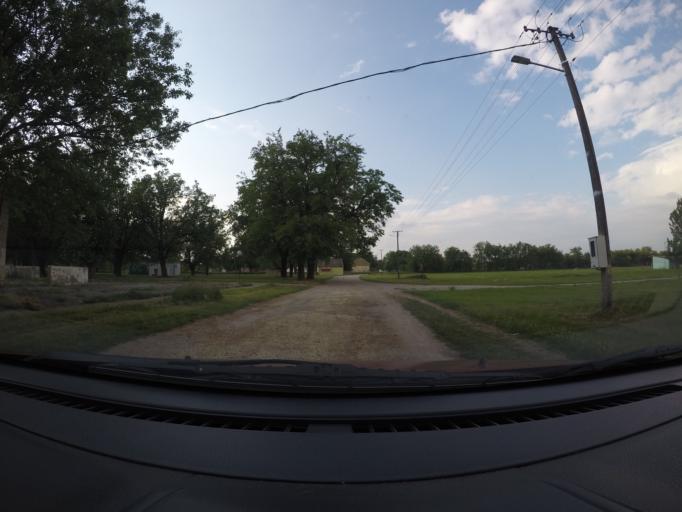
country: RS
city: Debeljaca
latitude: 45.0640
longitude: 20.6075
